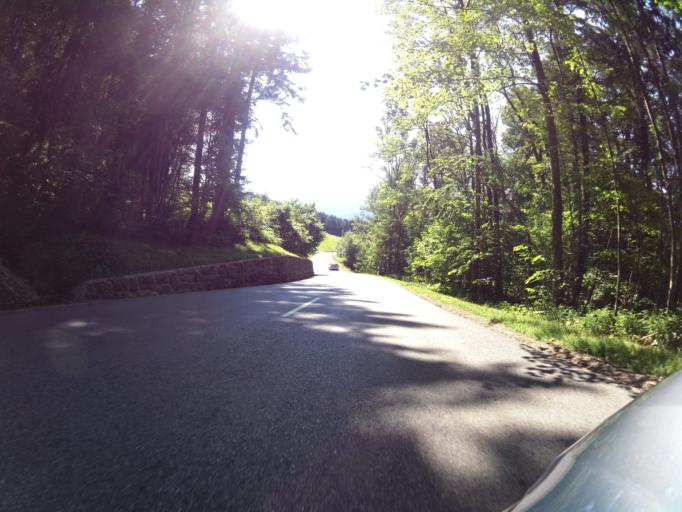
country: DE
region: Bavaria
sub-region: Upper Bavaria
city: Berchtesgaden
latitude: 47.6312
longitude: 13.0258
